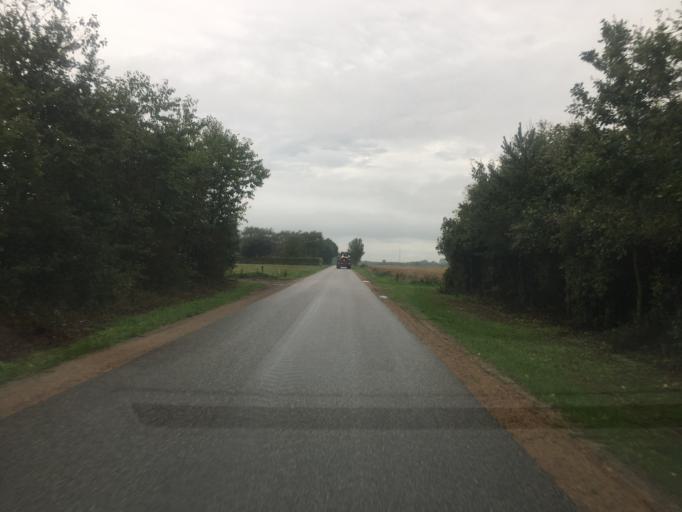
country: DK
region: South Denmark
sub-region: Tonder Kommune
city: Logumkloster
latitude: 55.0275
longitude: 9.0331
